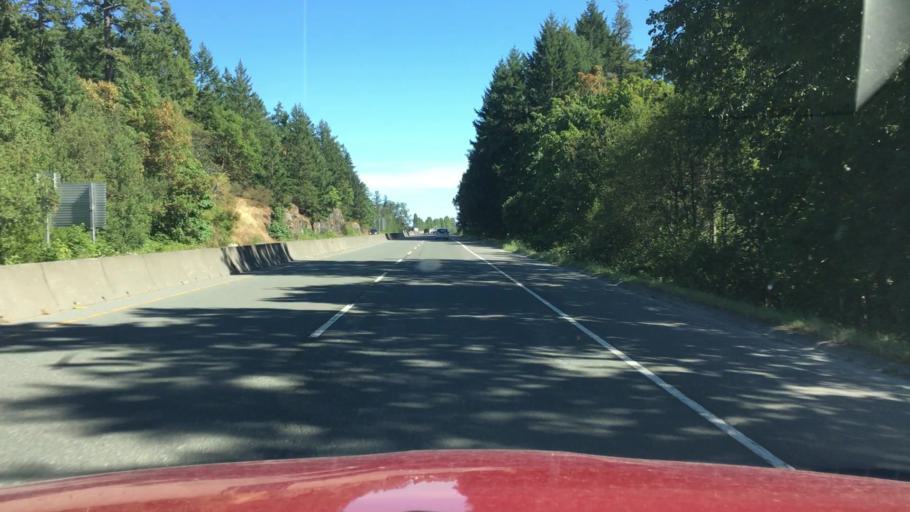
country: CA
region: British Columbia
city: North Saanich
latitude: 48.6689
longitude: -123.4245
